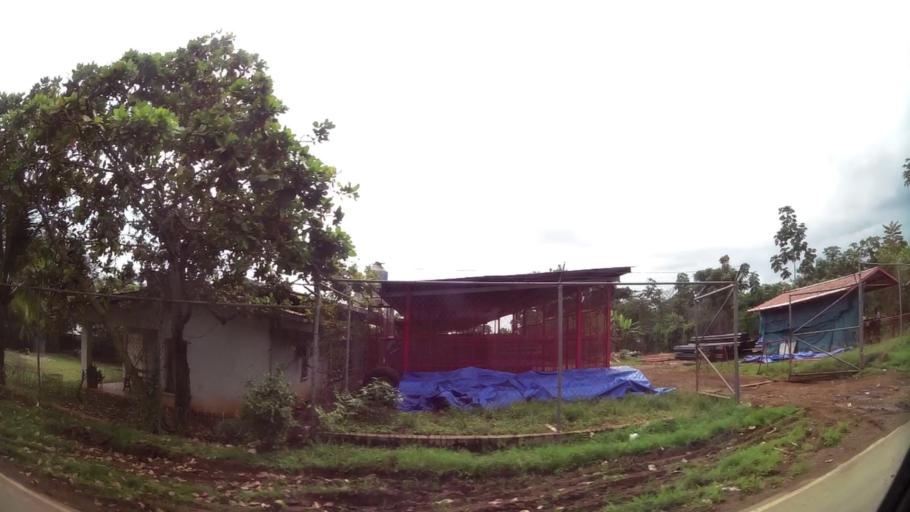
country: PA
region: Panama
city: Tocumen
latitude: 9.1088
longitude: -79.3820
